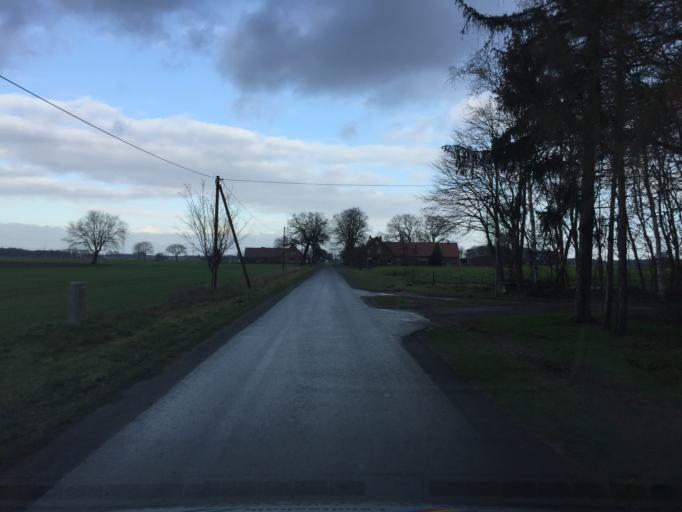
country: DE
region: Lower Saxony
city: Steyerberg
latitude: 52.5181
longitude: 9.0002
